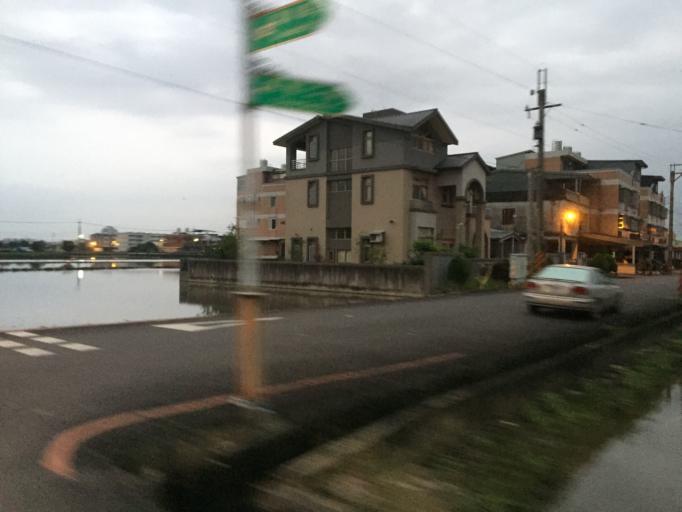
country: TW
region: Taiwan
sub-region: Yilan
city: Yilan
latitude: 24.7659
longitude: 121.7389
